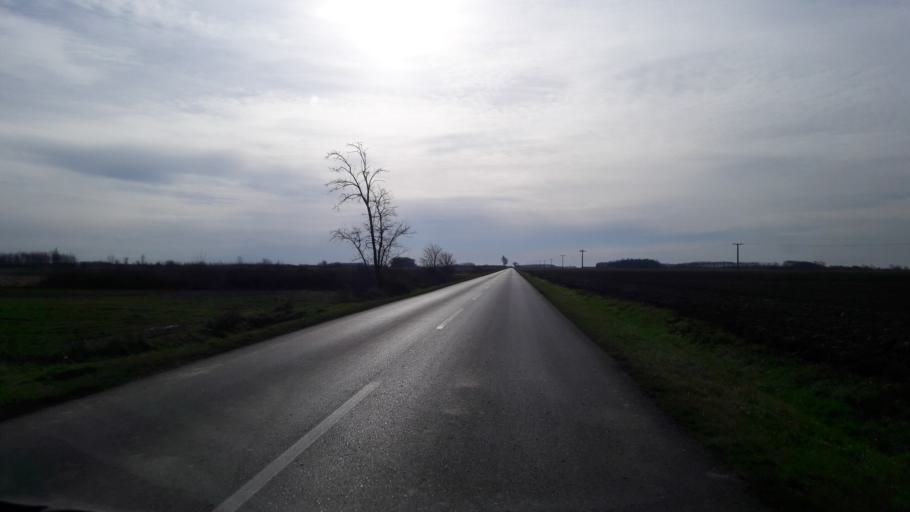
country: HR
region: Osjecko-Baranjska
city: Semeljci
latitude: 45.3390
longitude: 18.5575
